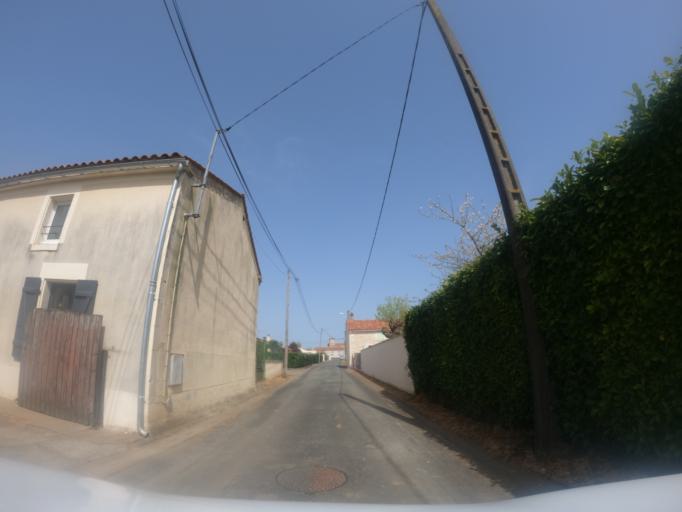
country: FR
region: Pays de la Loire
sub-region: Departement de la Vendee
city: Vix
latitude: 46.3901
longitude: -0.8072
